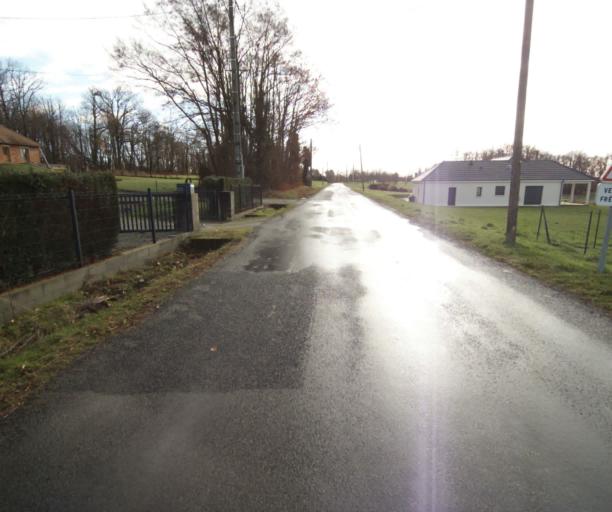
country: FR
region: Limousin
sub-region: Departement de la Correze
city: Saint-Mexant
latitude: 45.2812
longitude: 1.6021
